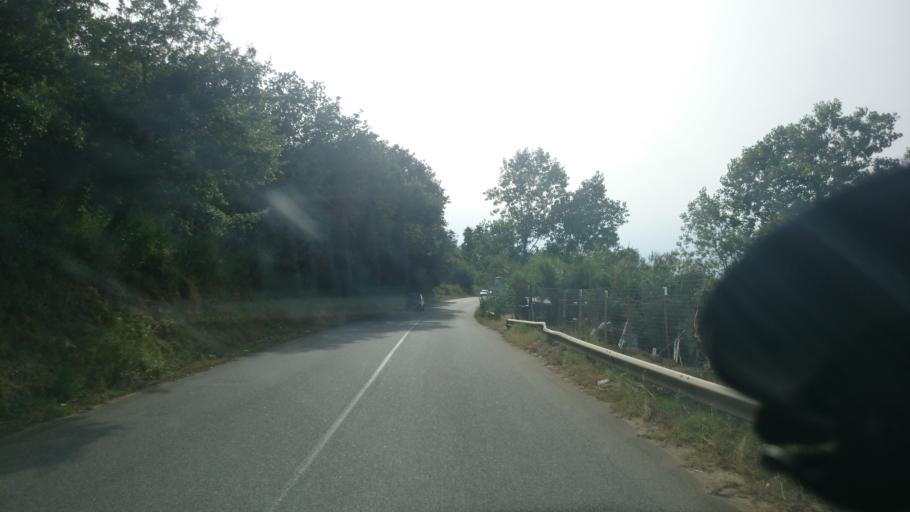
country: IT
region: Calabria
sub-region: Provincia di Vibo-Valentia
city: Briatico
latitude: 38.7208
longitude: 16.0034
